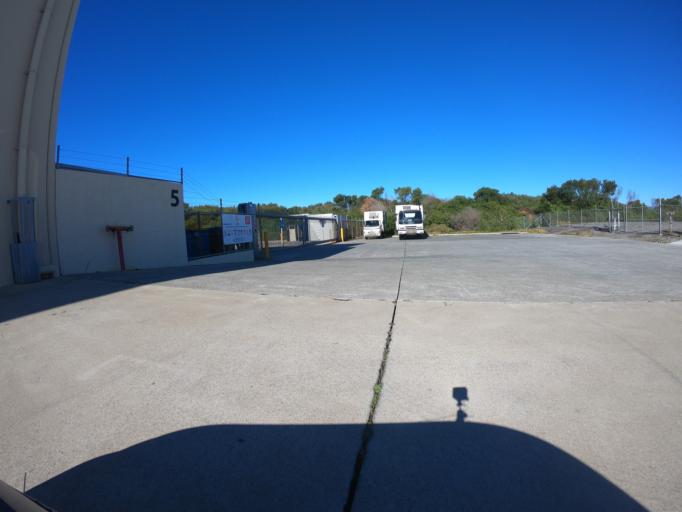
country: AU
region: New South Wales
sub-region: Wollongong
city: Port Kembla
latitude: -34.4982
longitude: 150.8932
